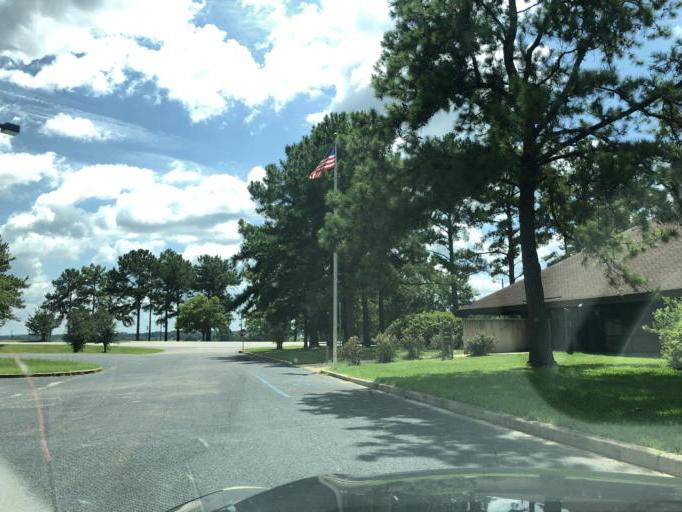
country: US
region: Alabama
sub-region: Barbour County
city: Eufaula
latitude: 31.9882
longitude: -85.1136
